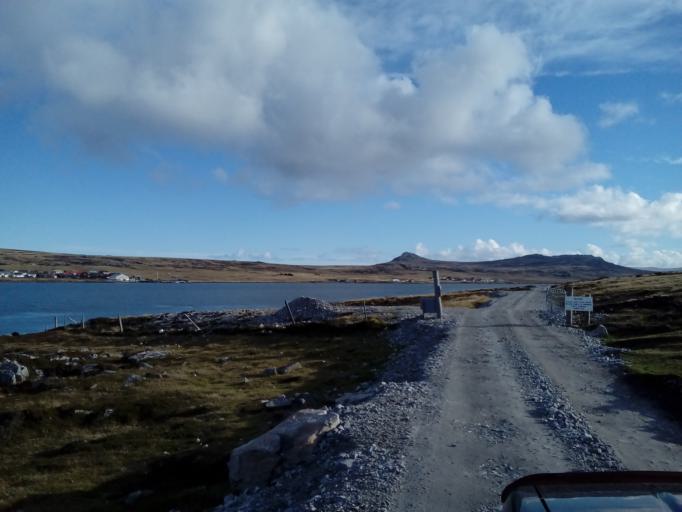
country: FK
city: Stanley
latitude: -51.6828
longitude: -57.8840
